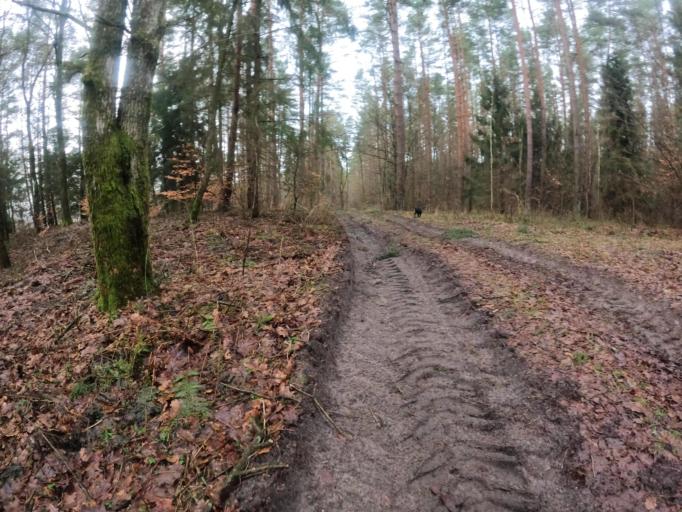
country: PL
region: West Pomeranian Voivodeship
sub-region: Powiat slawienski
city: Slawno
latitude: 54.2442
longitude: 16.6897
